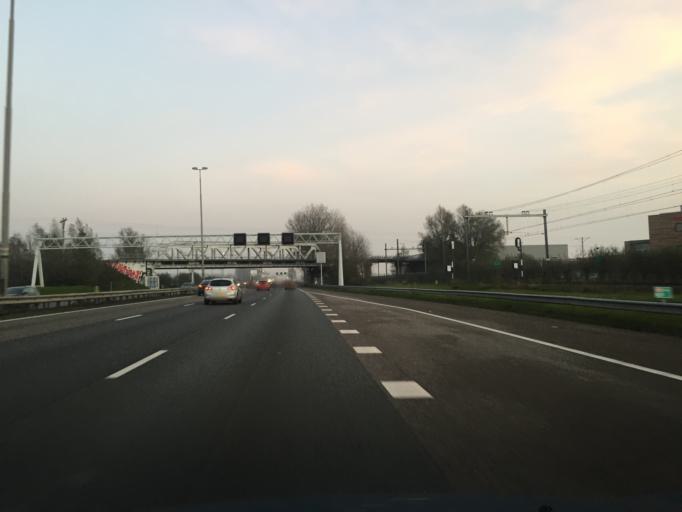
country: NL
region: South Holland
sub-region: Gemeente Pijnacker-Nootdorp
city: Pijnacker
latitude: 52.0528
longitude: 4.4092
